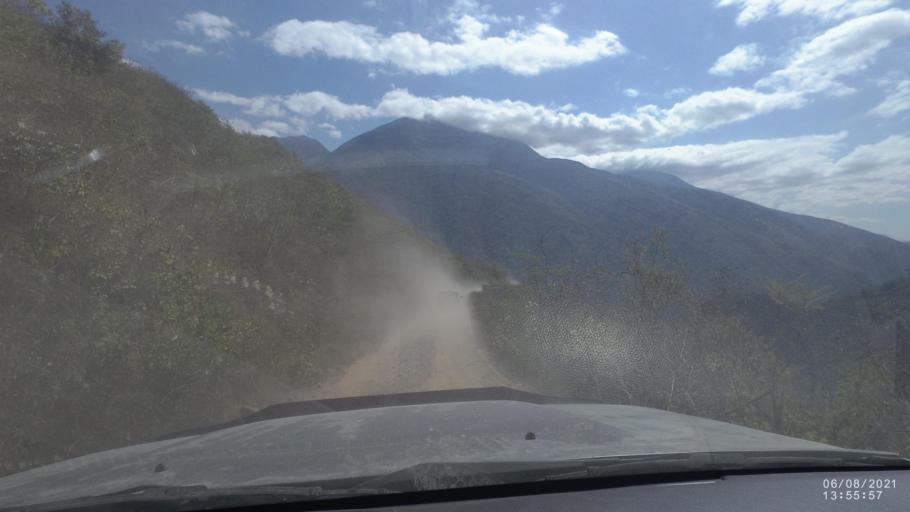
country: BO
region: La Paz
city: Quime
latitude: -16.6462
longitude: -66.7289
